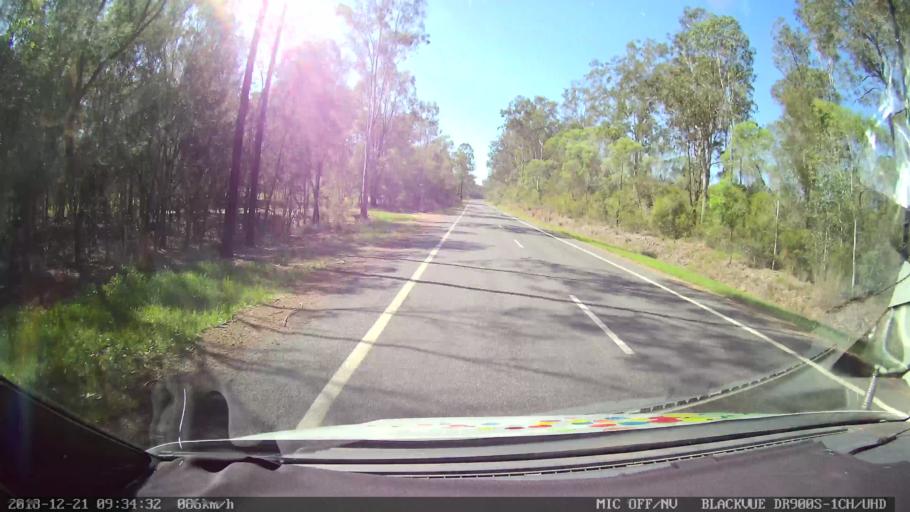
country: AU
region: New South Wales
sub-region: Clarence Valley
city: Grafton
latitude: -29.4990
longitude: 152.9805
